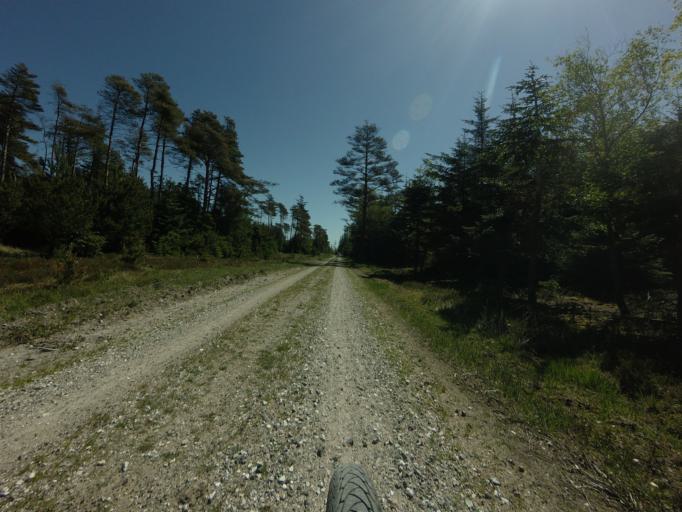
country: DK
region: North Denmark
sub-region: Jammerbugt Kommune
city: Pandrup
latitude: 57.2350
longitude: 9.5884
